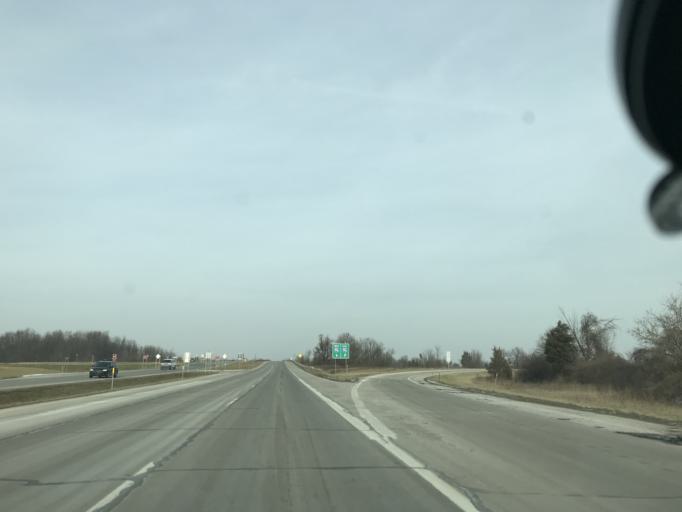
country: US
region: Michigan
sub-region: Ionia County
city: Lake Odessa
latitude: 42.8757
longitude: -85.0749
